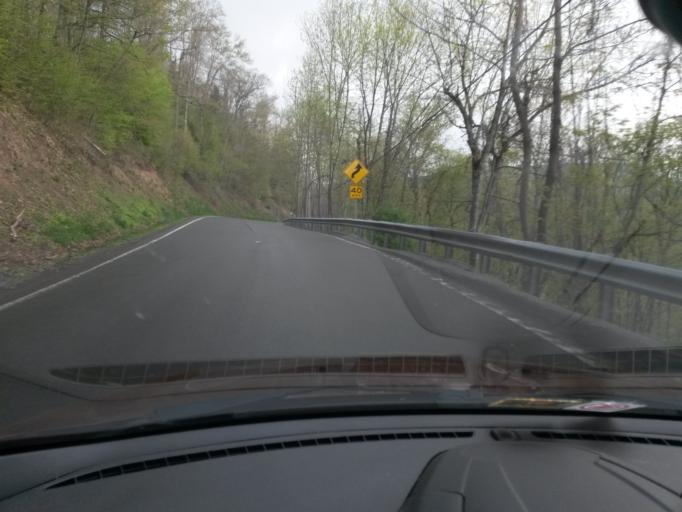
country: US
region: Virginia
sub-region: Highland County
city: Monterey
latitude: 38.5953
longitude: -79.8473
